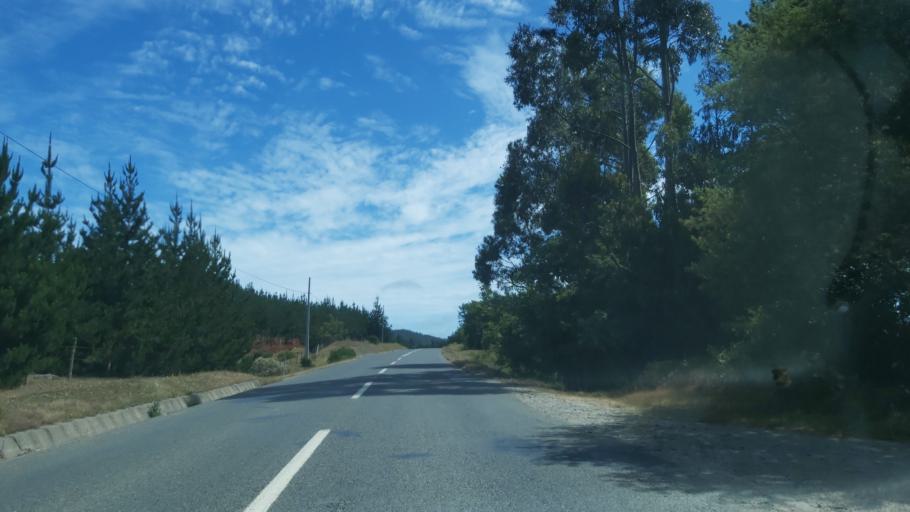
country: CL
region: Maule
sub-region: Provincia de Talca
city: Constitucion
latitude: -35.5563
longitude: -72.5834
